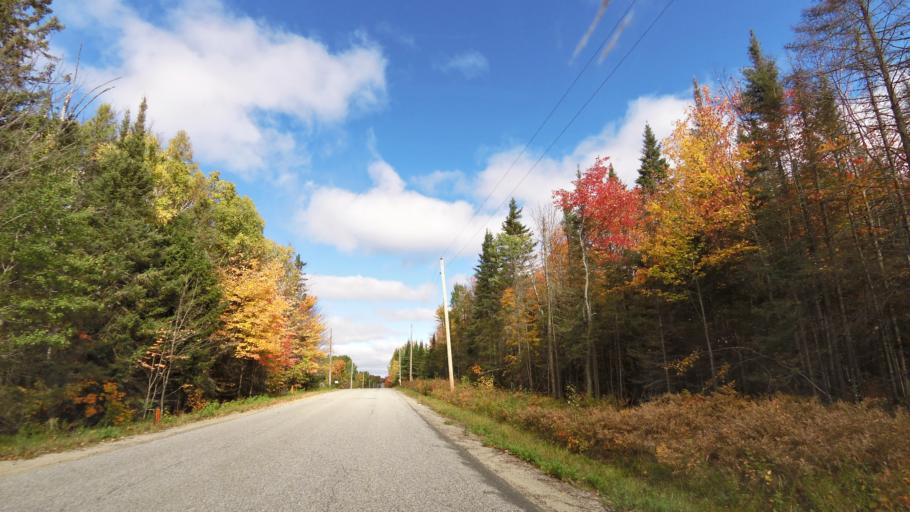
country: CA
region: Ontario
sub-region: Nipissing District
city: North Bay
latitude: 46.3605
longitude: -79.4871
